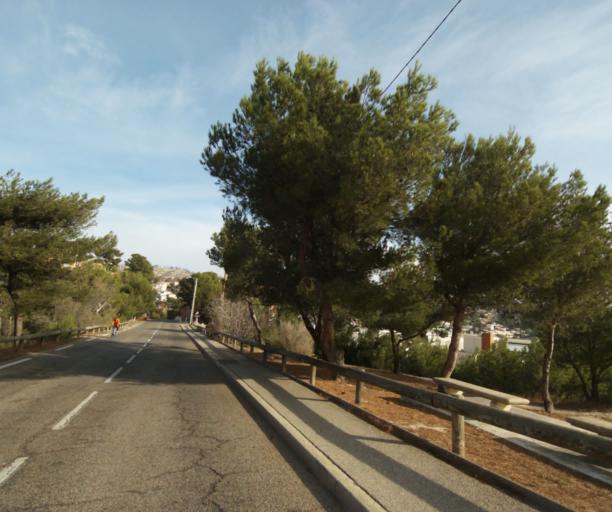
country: FR
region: Provence-Alpes-Cote d'Azur
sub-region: Departement des Bouches-du-Rhone
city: Carry-le-Rouet
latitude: 43.3319
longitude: 5.1703
